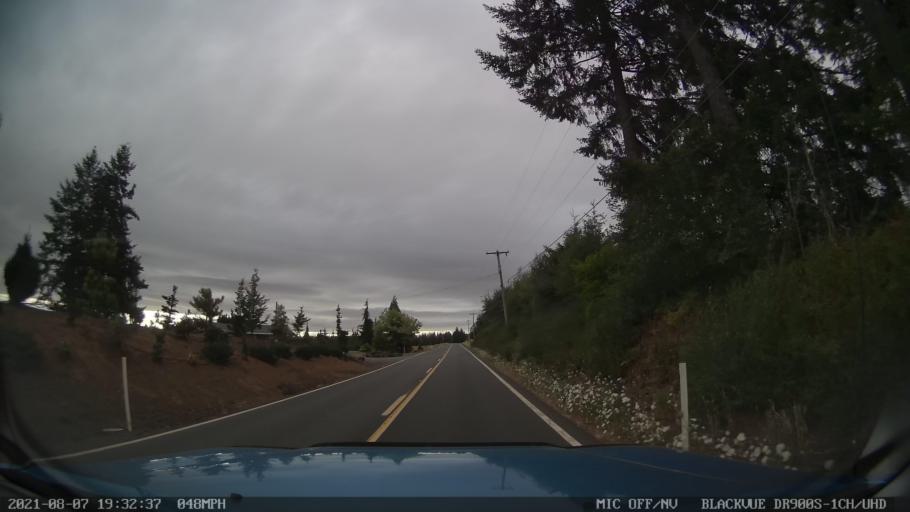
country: US
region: Oregon
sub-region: Linn County
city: Lyons
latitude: 44.9013
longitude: -122.6459
